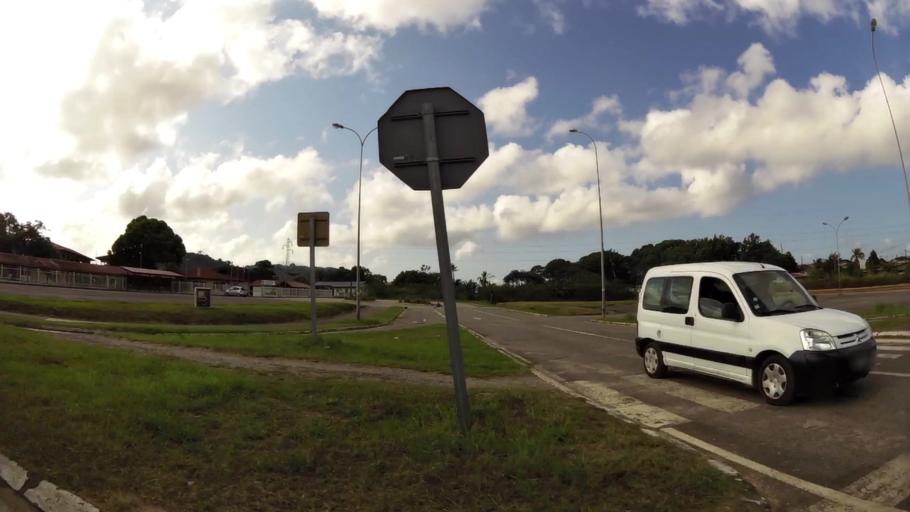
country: GF
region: Guyane
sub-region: Guyane
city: Cayenne
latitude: 4.9278
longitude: -52.3185
